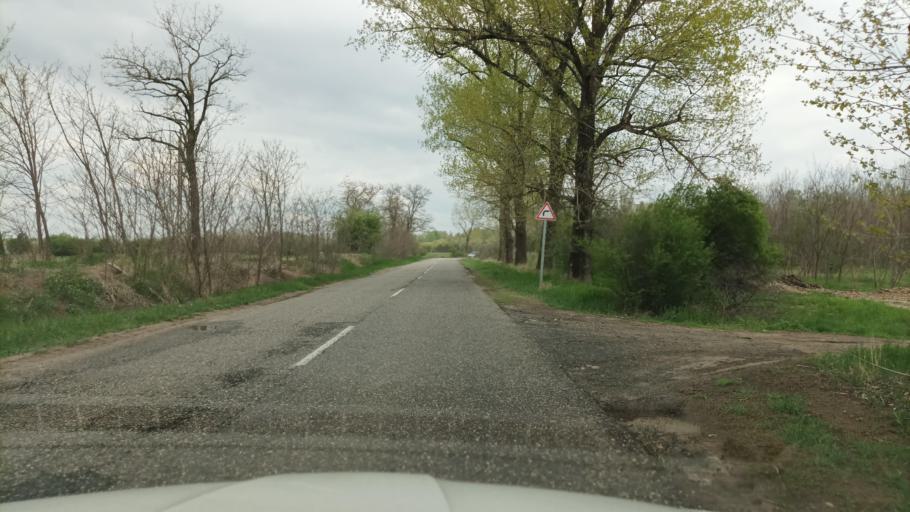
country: HU
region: Pest
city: Tortel
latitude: 47.0851
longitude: 19.8749
